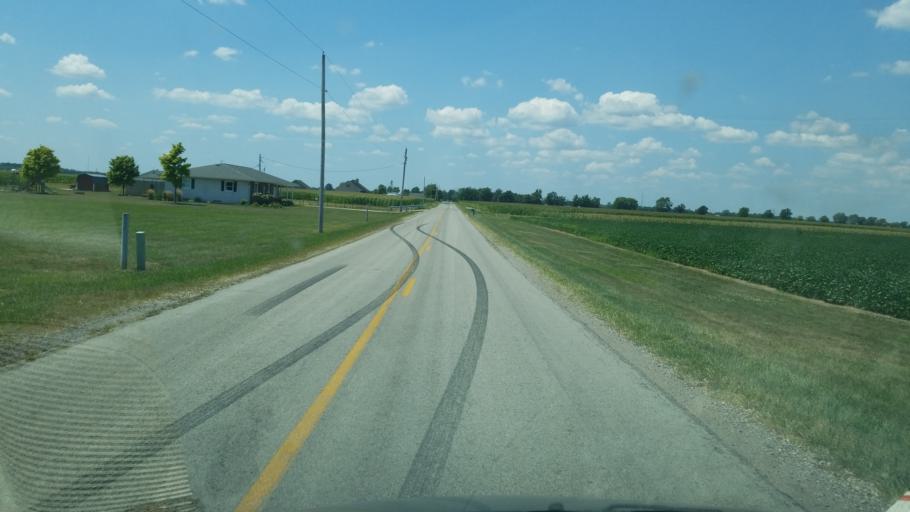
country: US
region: Ohio
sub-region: Madison County
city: Plain City
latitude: 40.0410
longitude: -83.3687
